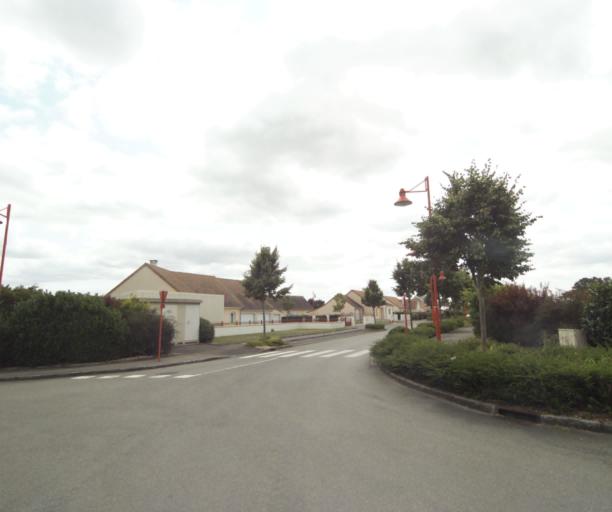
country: FR
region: Pays de la Loire
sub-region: Departement de la Sarthe
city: Sable-sur-Sarthe
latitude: 47.8520
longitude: -0.3511
